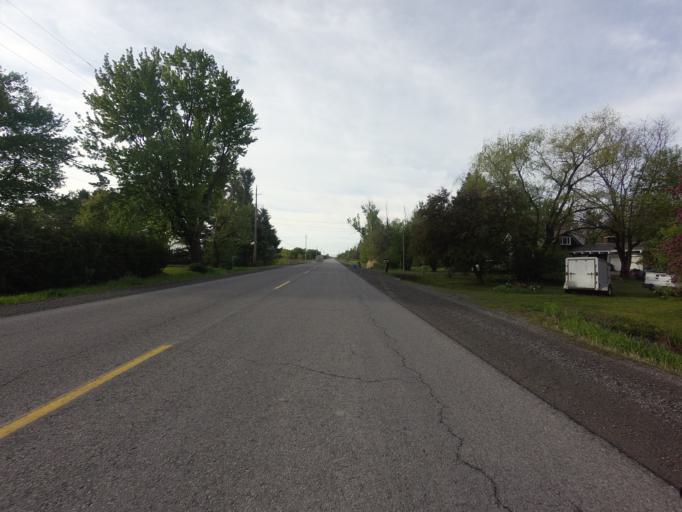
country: CA
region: Ontario
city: Ottawa
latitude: 45.3112
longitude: -75.4597
